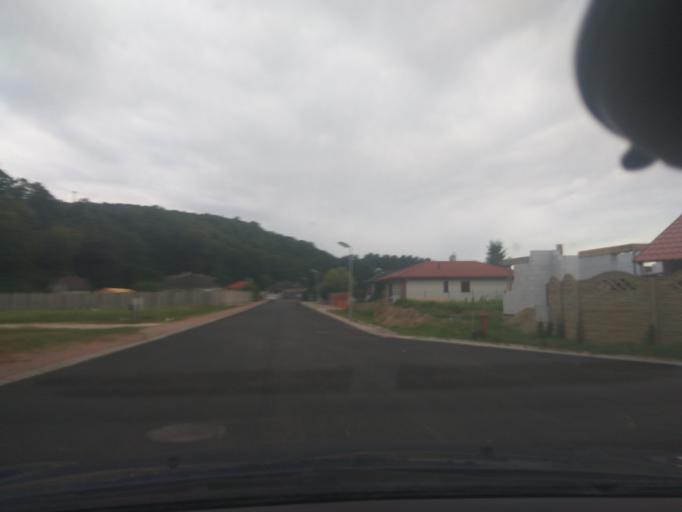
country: SK
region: Trenciansky
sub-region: Okres Nove Mesto nad Vahom
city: Nove Mesto nad Vahom
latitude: 48.6946
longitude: 17.8820
